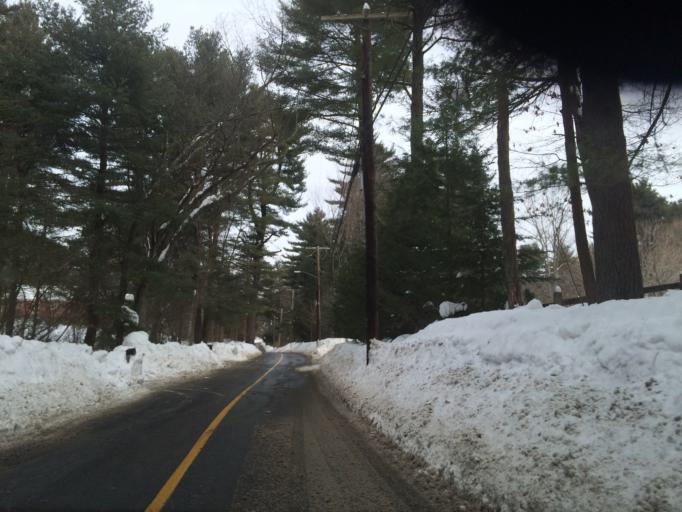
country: US
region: Massachusetts
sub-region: Middlesex County
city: Weston
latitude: 42.3867
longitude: -71.3225
